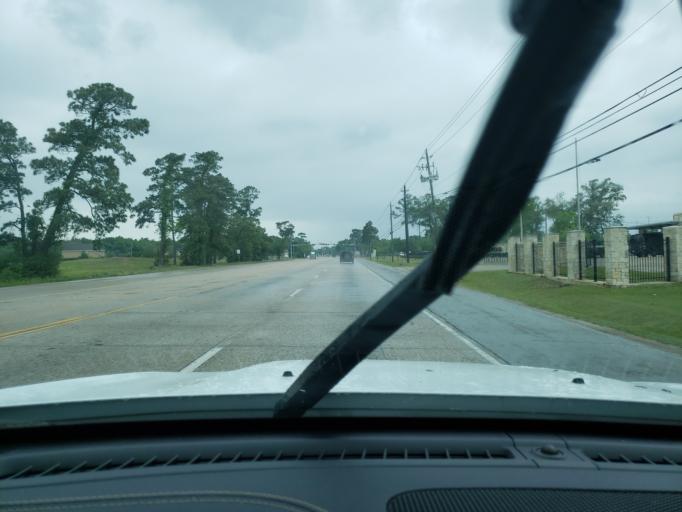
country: US
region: Texas
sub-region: Chambers County
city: Mont Belvieu
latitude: 29.7849
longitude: -94.9120
